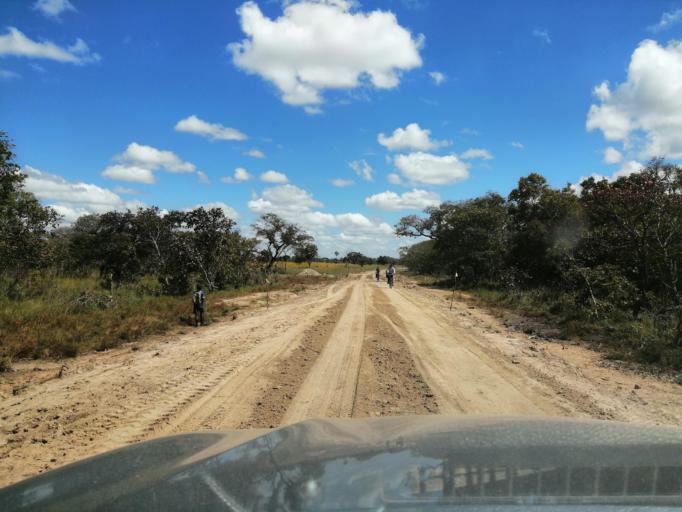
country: ZM
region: Central
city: Mumbwa
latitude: -14.5762
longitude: 27.2578
